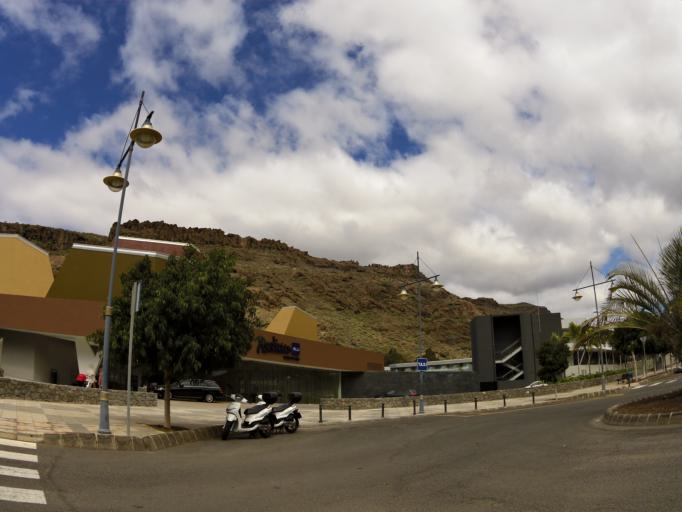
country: ES
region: Canary Islands
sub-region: Provincia de Las Palmas
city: Puerto Rico
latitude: 27.8255
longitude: -15.7574
